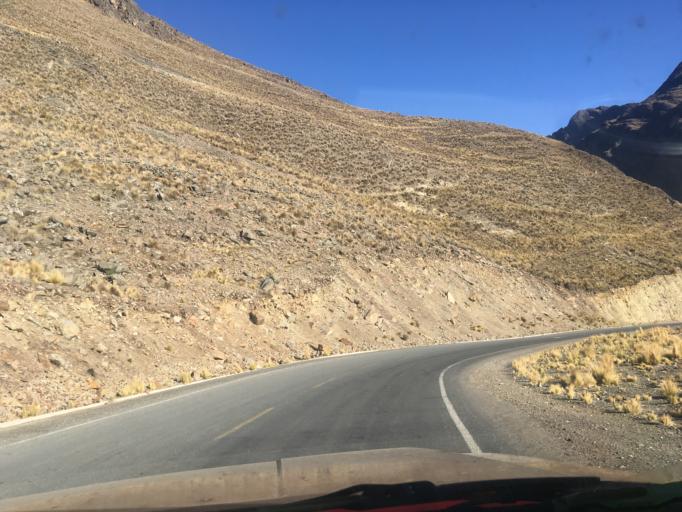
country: BO
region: La Paz
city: Quime
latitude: -17.0318
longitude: -67.2862
